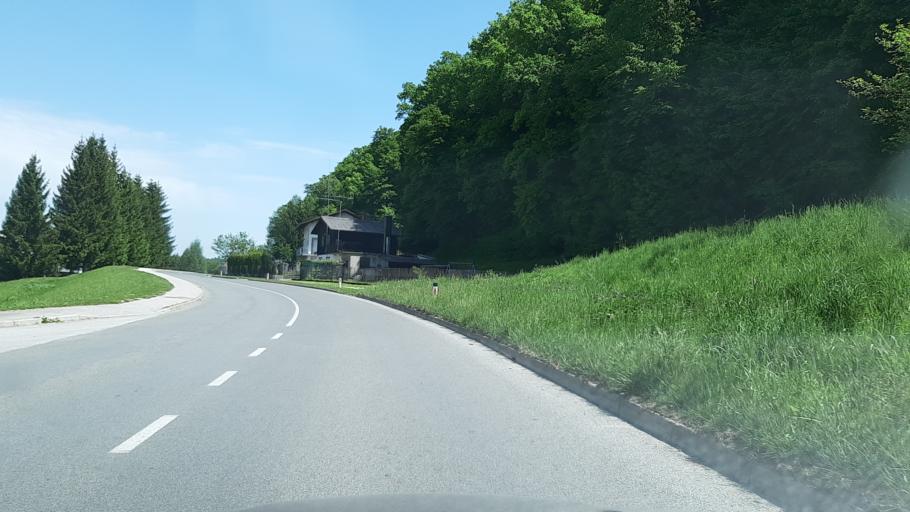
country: SI
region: Sentjur pri Celju
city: Sentjur
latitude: 46.2073
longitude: 15.4006
